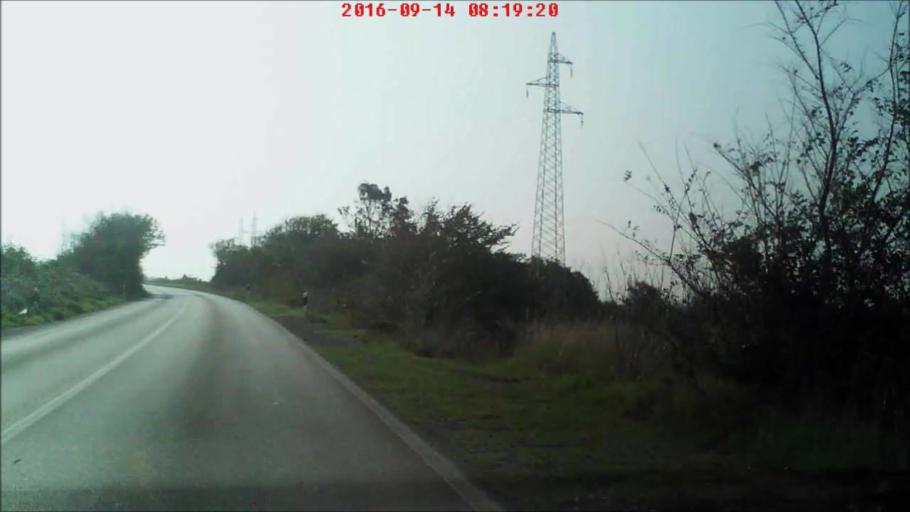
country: HR
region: Zadarska
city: Nin
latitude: 44.2335
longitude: 15.1890
